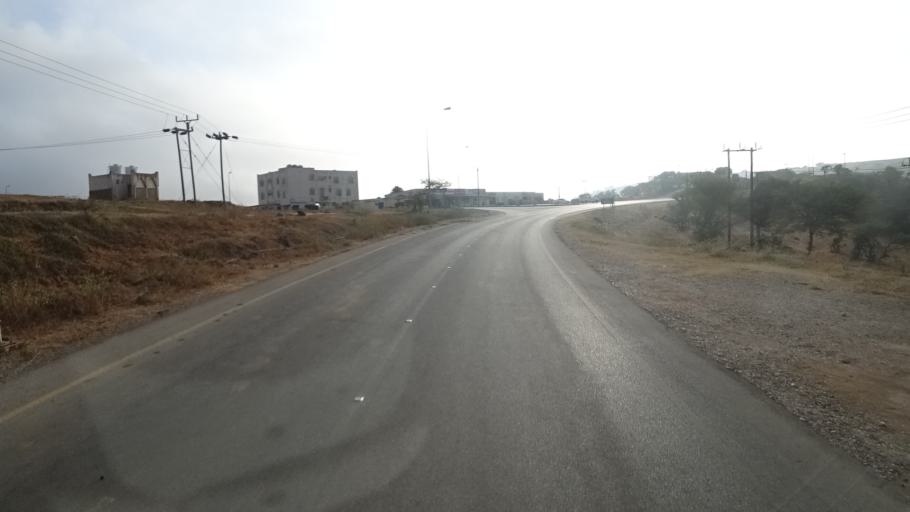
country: OM
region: Zufar
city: Salalah
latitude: 17.1187
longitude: 53.9886
